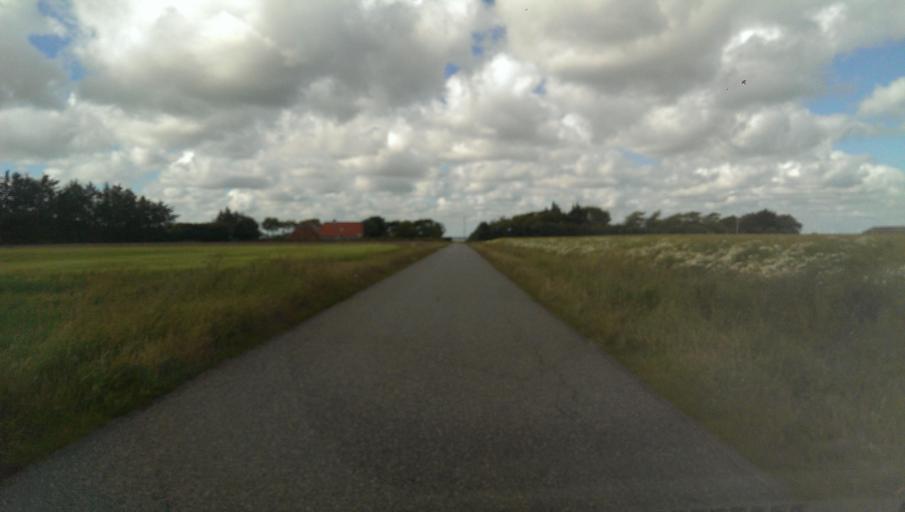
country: DK
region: Central Jutland
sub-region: Holstebro Kommune
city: Ulfborg
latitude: 56.2733
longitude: 8.2474
